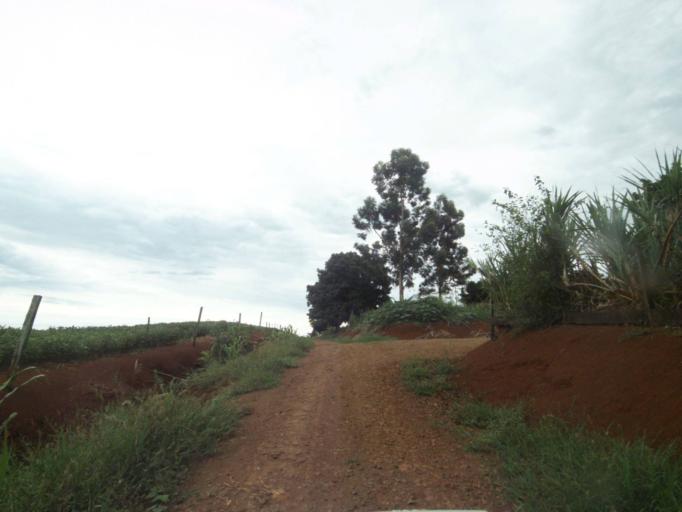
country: BR
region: Parana
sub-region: Guaraniacu
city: Guaraniacu
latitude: -24.9187
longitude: -52.9391
